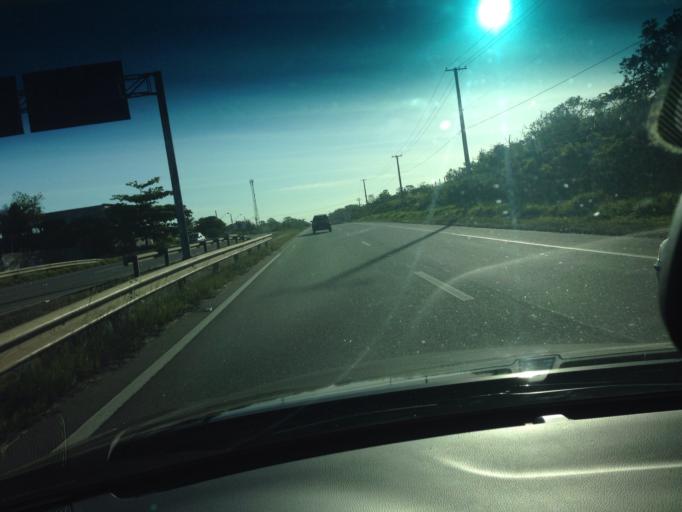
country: BR
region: Espirito Santo
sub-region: Viana
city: Viana
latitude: -20.5181
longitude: -40.3666
